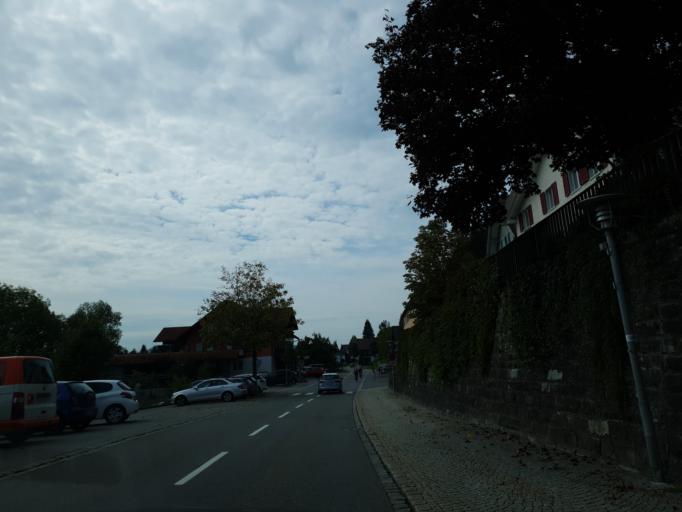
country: AT
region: Vorarlberg
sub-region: Politischer Bezirk Bregenz
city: Doren
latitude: 47.4923
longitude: 9.8792
